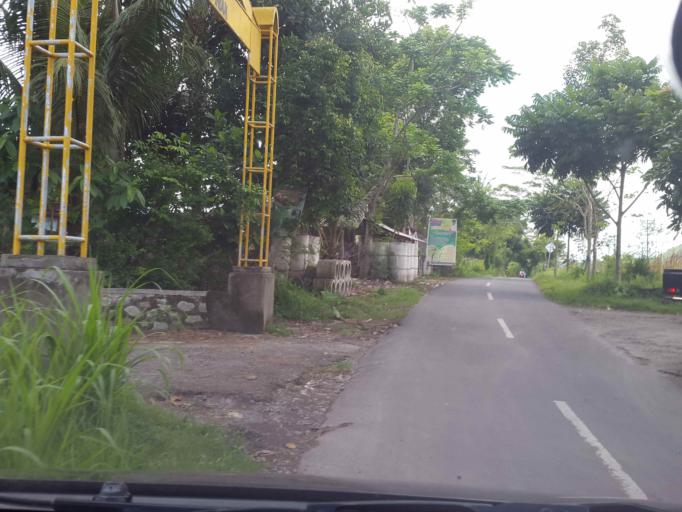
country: ID
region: West Nusa Tenggara
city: Ranggagata
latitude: -8.6951
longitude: 116.1443
